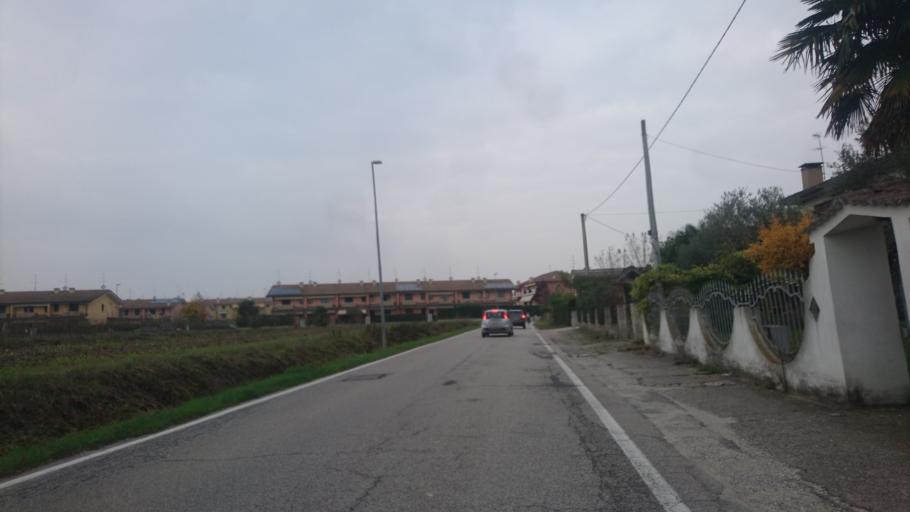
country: IT
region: Veneto
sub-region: Provincia di Venezia
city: Tombelle
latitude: 45.3931
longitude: 11.9801
